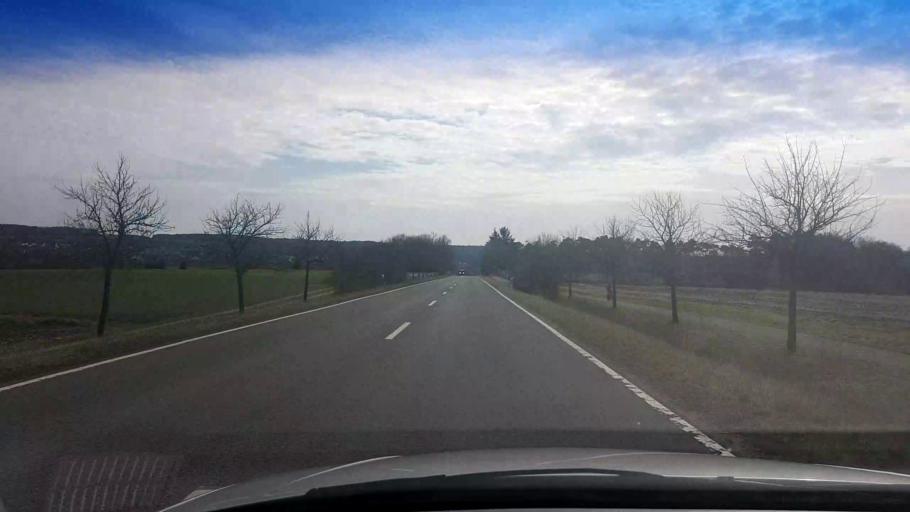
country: DE
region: Bavaria
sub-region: Upper Franconia
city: Frensdorf
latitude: 49.8299
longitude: 10.8683
